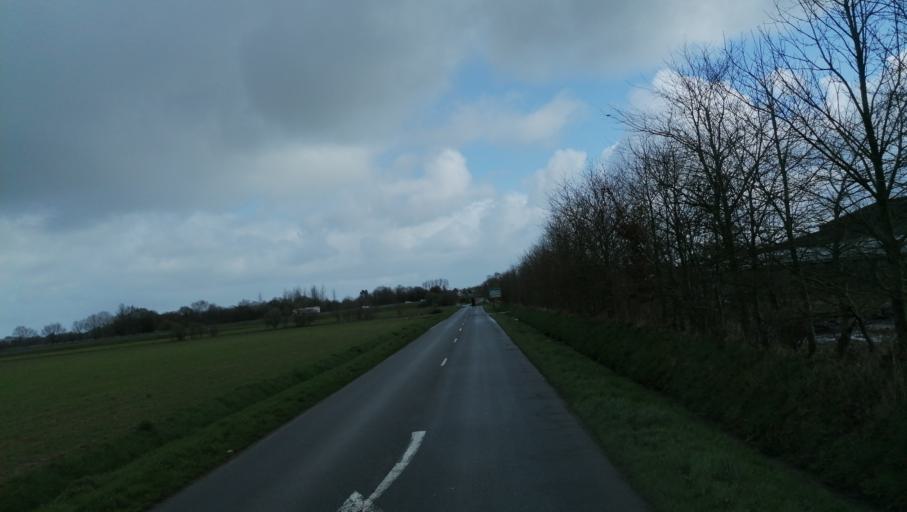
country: FR
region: Brittany
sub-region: Departement des Cotes-d'Armor
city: Plouagat
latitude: 48.5307
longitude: -3.0121
